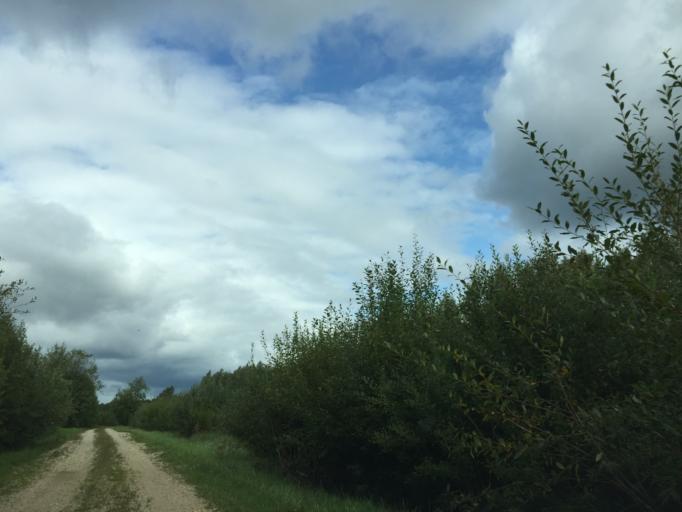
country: LV
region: Pargaujas
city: Stalbe
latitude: 57.4817
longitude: 24.9071
